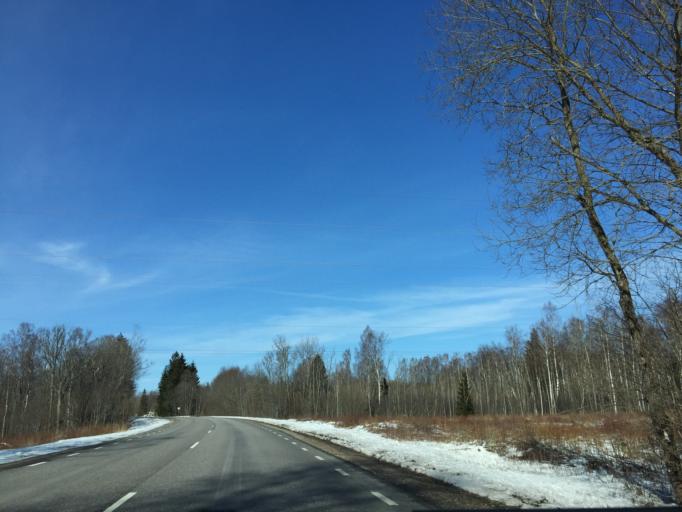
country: EE
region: Laeaene
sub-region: Lihula vald
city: Lihula
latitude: 58.6238
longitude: 23.6898
